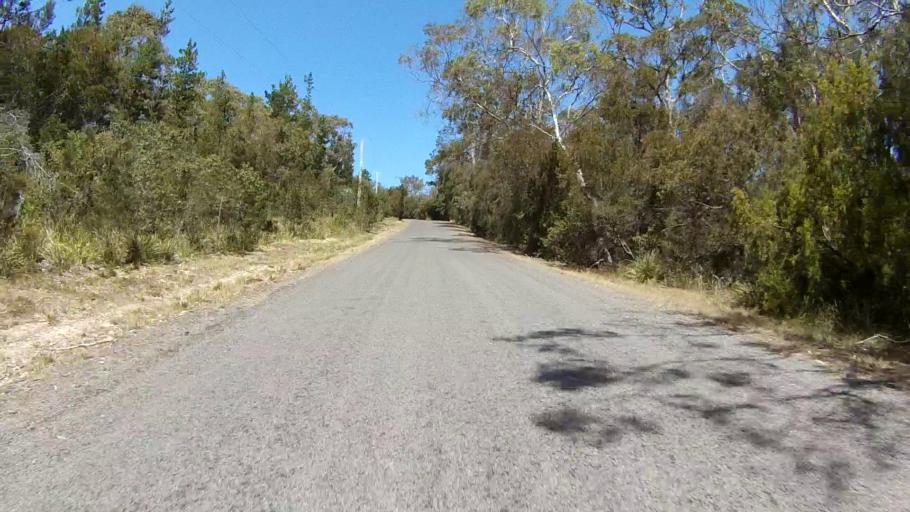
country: AU
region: Tasmania
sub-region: Clarence
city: Sandford
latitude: -43.0210
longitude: 147.4772
